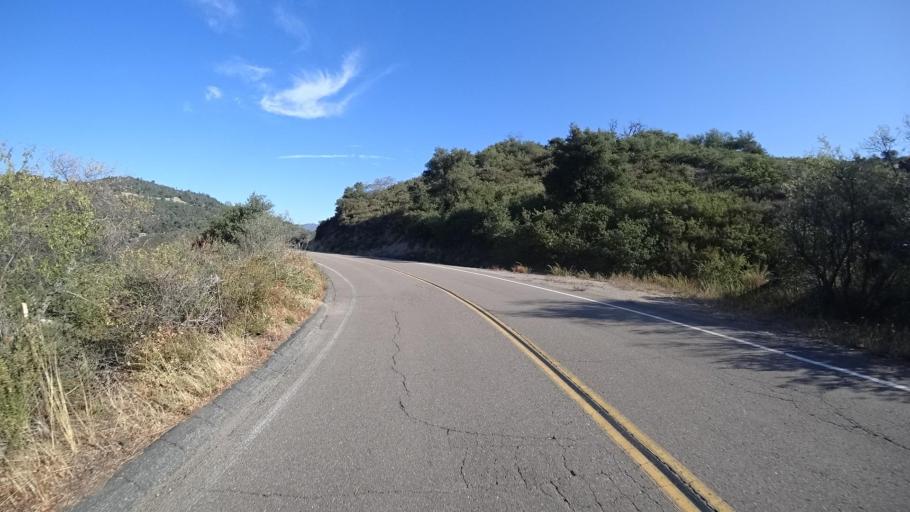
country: US
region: California
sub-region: Riverside County
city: Aguanga
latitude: 33.2706
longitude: -116.7826
